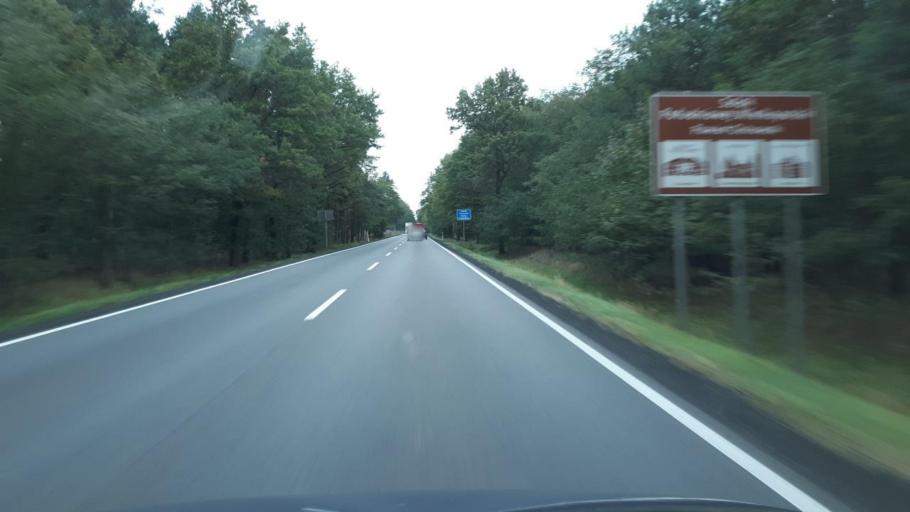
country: PL
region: Greater Poland Voivodeship
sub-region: Powiat ostrowski
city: Przygodzice
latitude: 51.4997
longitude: 17.8520
